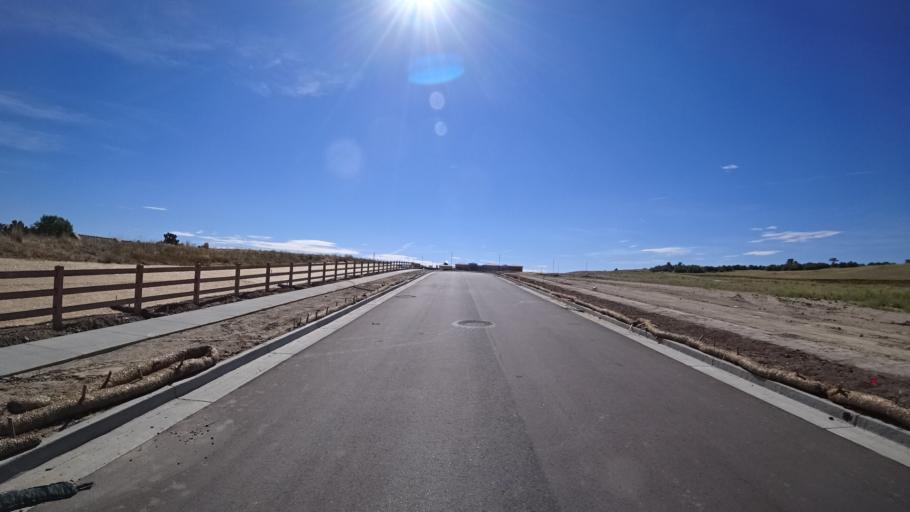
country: US
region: Colorado
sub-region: El Paso County
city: Gleneagle
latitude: 39.0257
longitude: -104.7970
